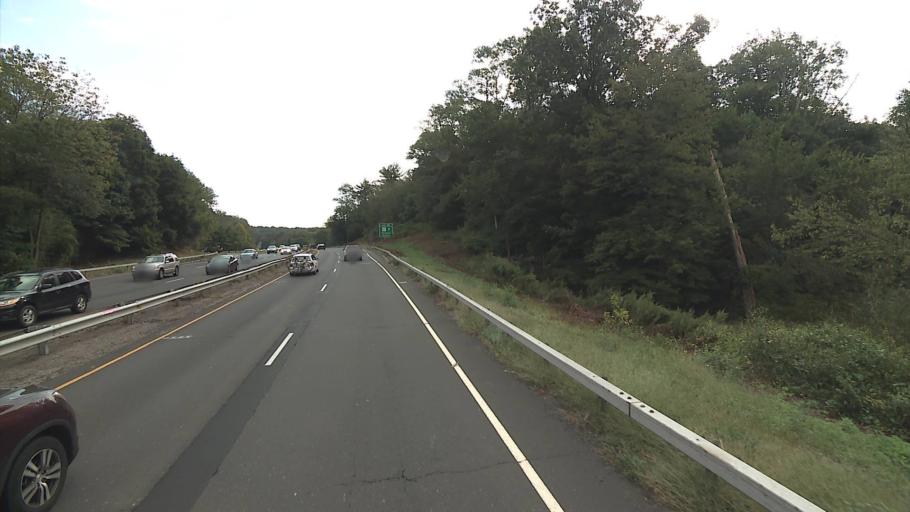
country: US
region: Connecticut
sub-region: Fairfield County
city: Westport
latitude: 41.1633
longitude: -73.3613
